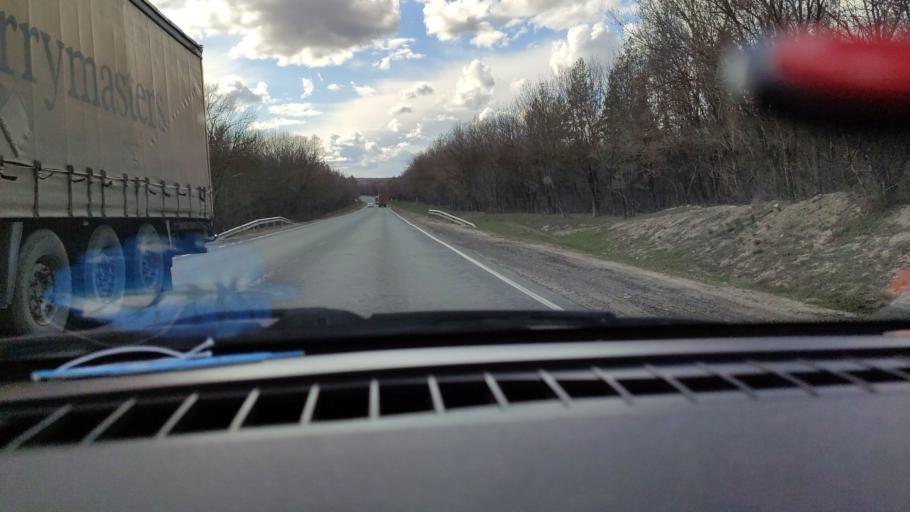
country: RU
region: Saratov
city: Vol'sk
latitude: 52.1058
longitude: 47.4336
